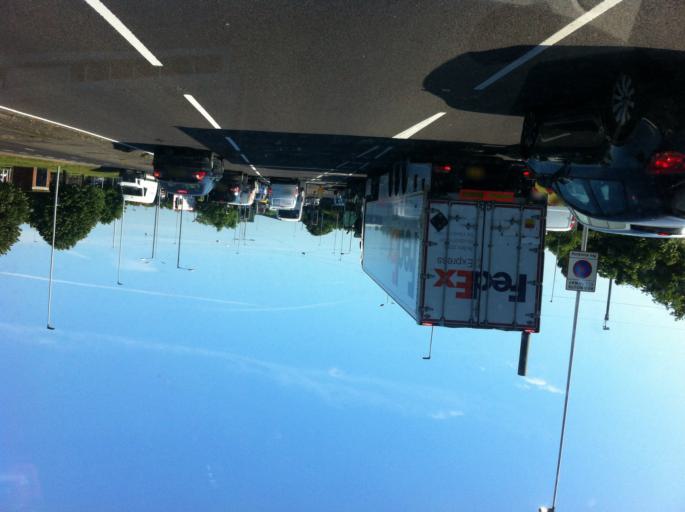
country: GB
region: England
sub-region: Greater London
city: Feltham
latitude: 51.4731
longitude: -0.4053
